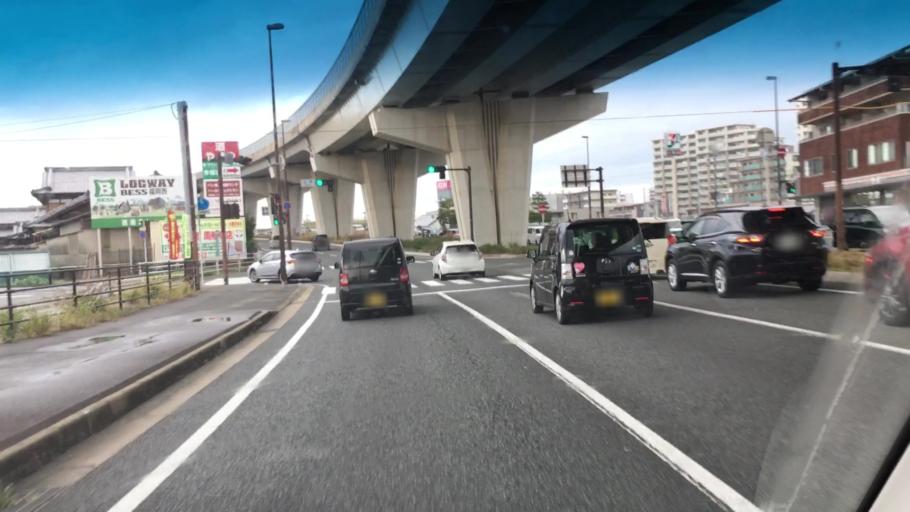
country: JP
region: Fukuoka
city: Maebaru-chuo
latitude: 33.5746
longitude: 130.2641
